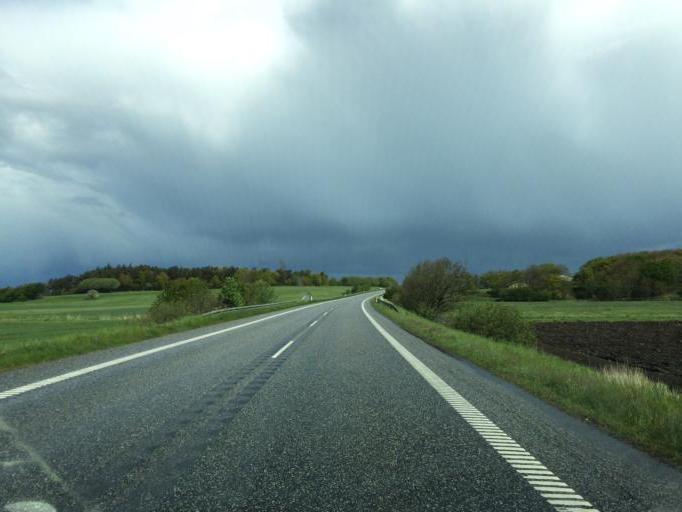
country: DK
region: Central Jutland
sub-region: Skive Kommune
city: Hojslev
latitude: 56.5610
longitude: 9.1109
